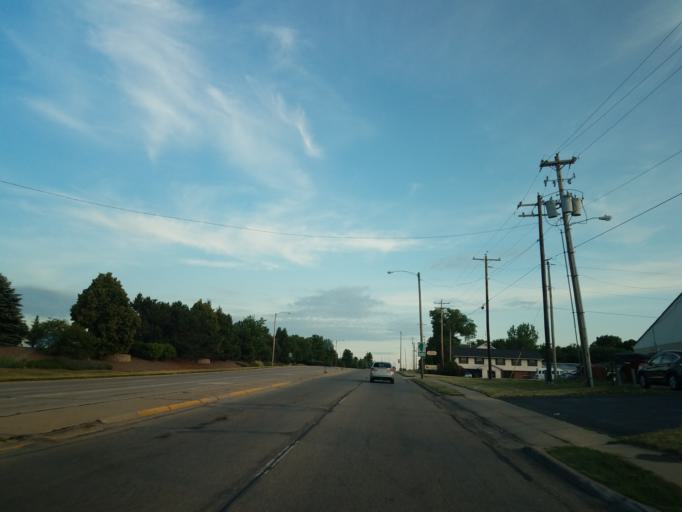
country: US
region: Illinois
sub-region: McLean County
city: Bloomington
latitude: 40.4567
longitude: -88.9929
